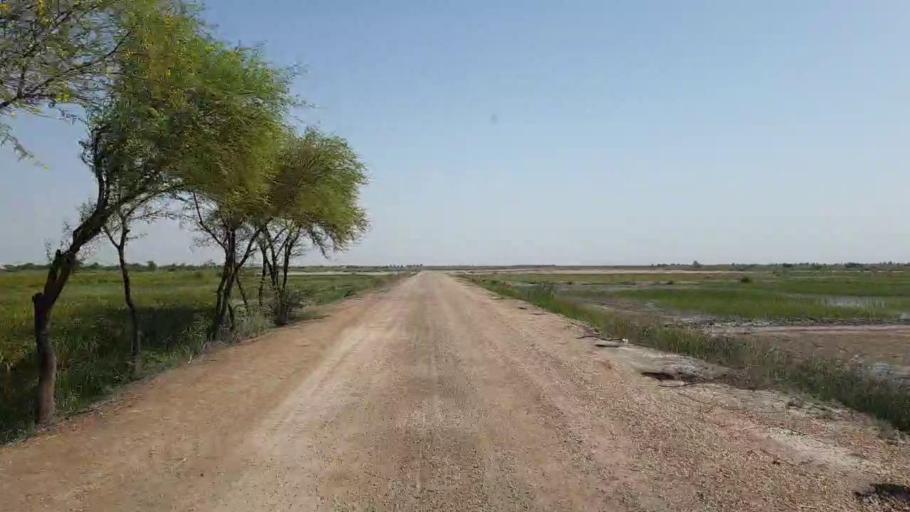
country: PK
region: Sindh
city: Tando Bago
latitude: 24.7309
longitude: 69.0282
